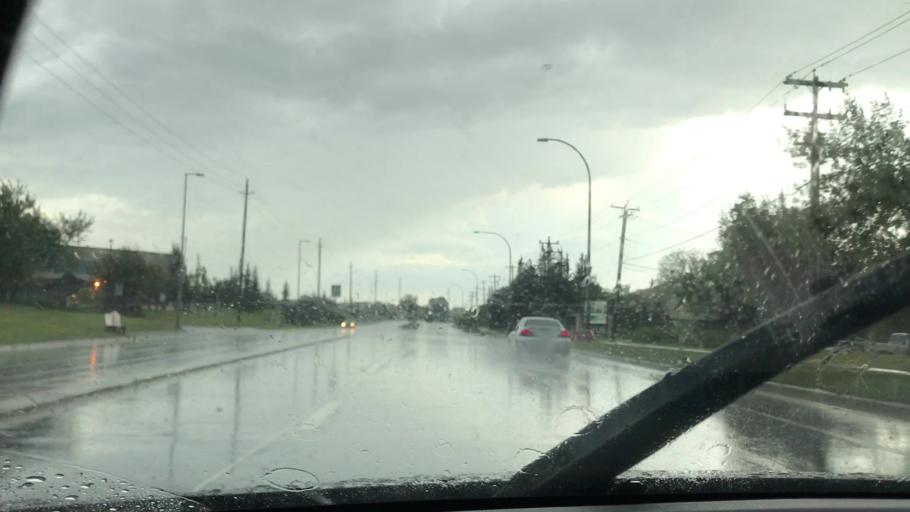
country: CA
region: Alberta
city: Edmonton
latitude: 53.4912
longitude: -113.4465
